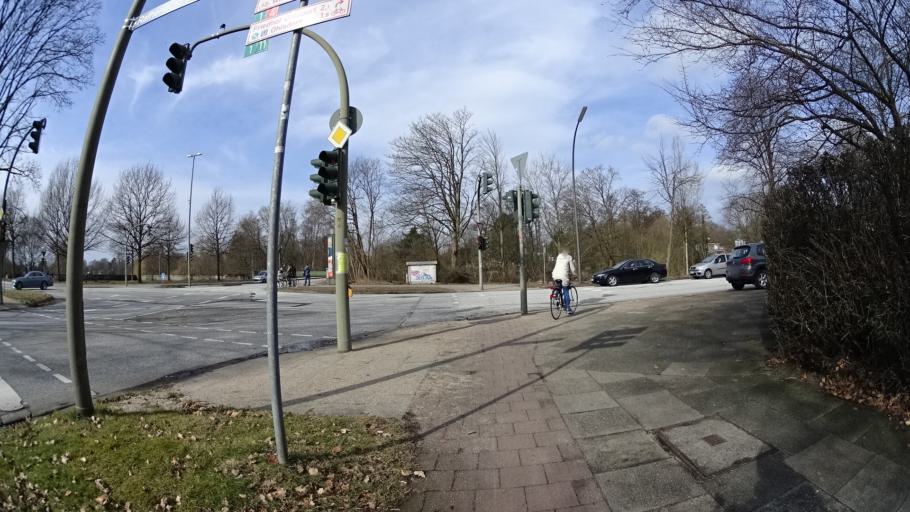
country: DE
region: Hamburg
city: Alsterdorf
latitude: 53.6116
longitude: 10.0107
